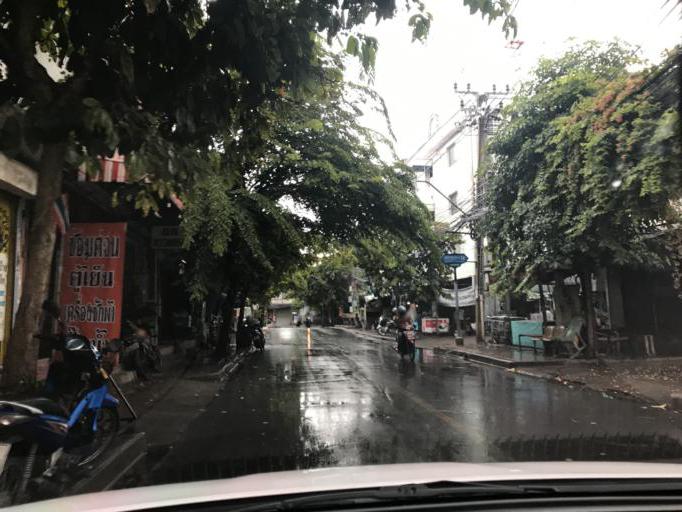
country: TH
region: Bangkok
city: Phasi Charoen
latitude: 13.7223
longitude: 100.4398
